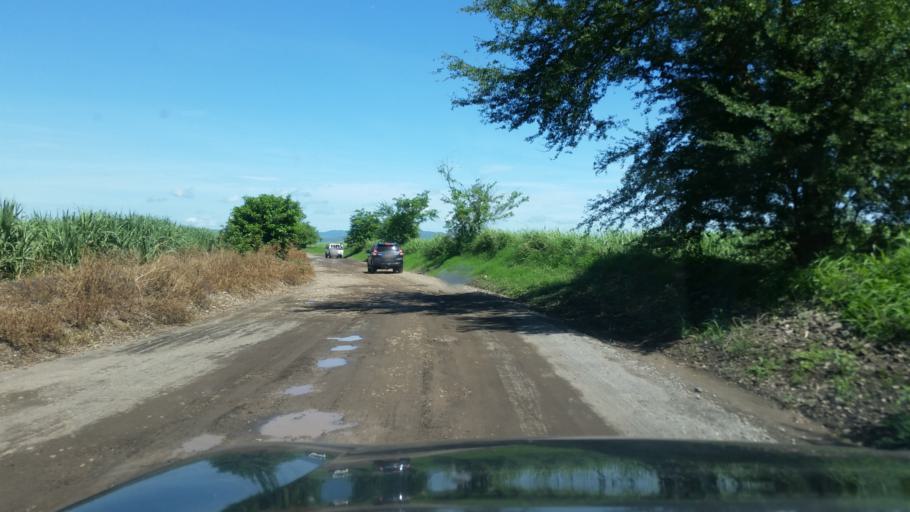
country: NI
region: Chinandega
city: Puerto Morazan
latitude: 12.7740
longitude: -87.1017
